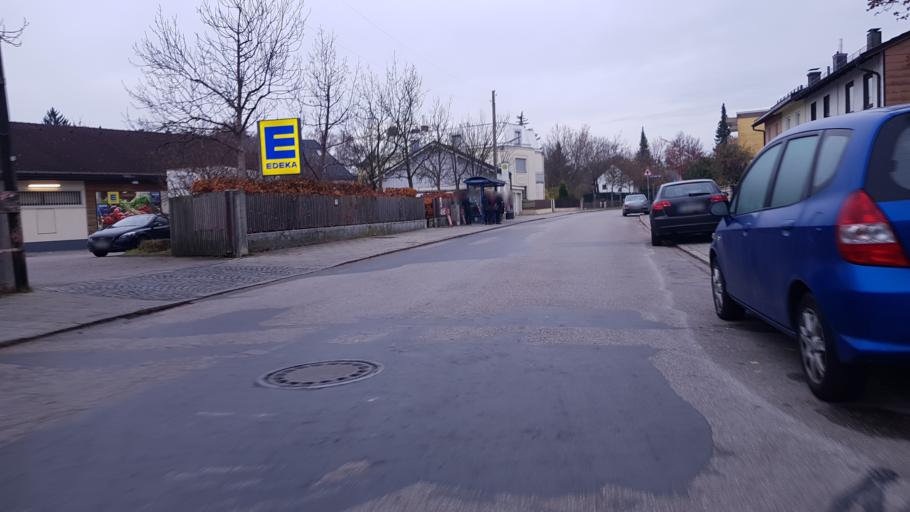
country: DE
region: Bavaria
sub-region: Upper Bavaria
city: Bogenhausen
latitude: 48.1112
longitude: 11.6273
